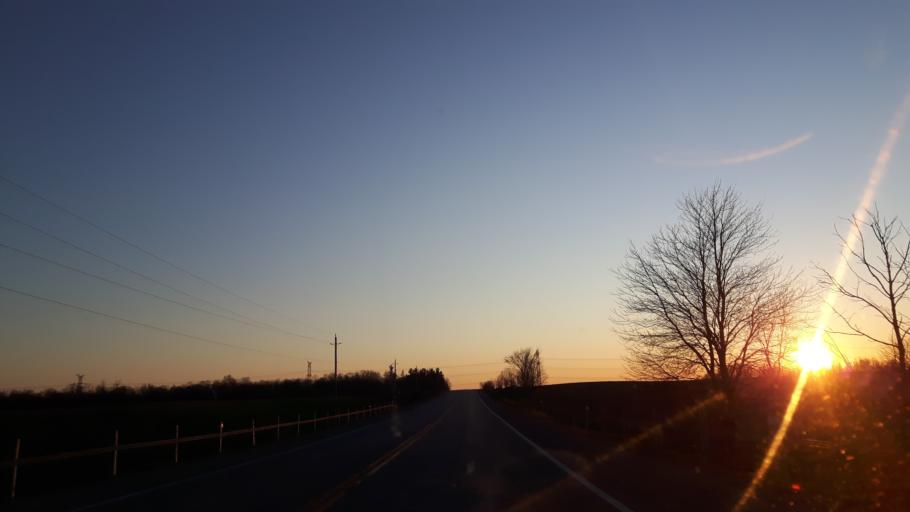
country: CA
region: Ontario
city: Bluewater
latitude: 43.5869
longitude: -81.6235
